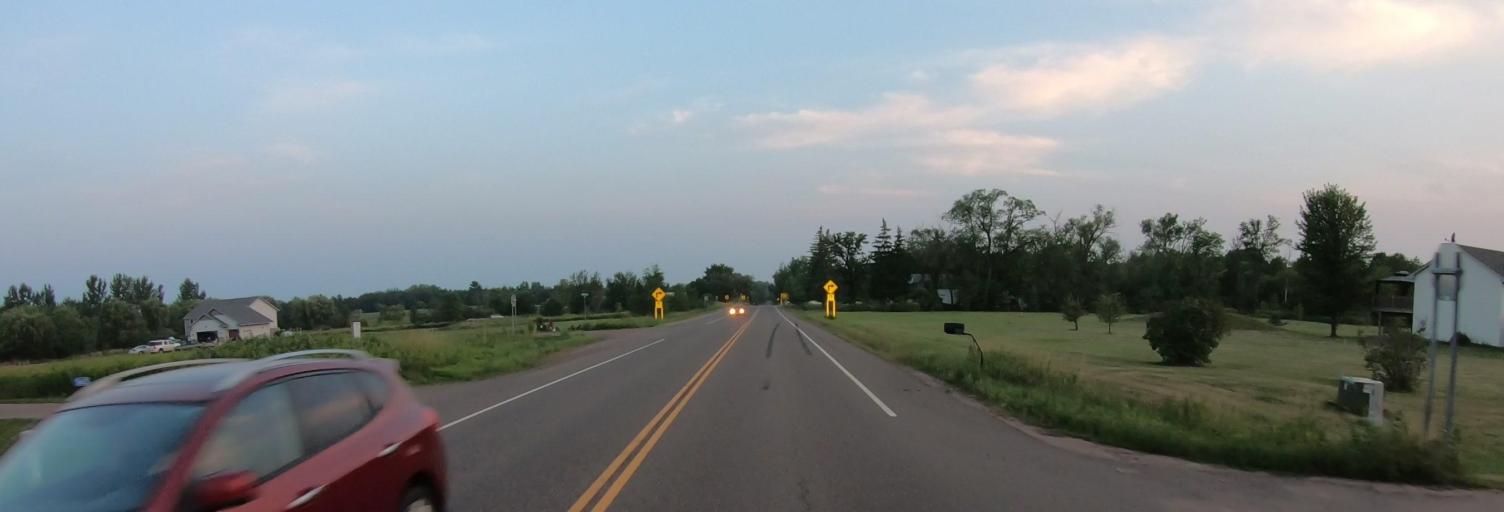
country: US
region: Minnesota
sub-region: Pine County
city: Rock Creek
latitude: 45.7683
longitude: -92.9602
